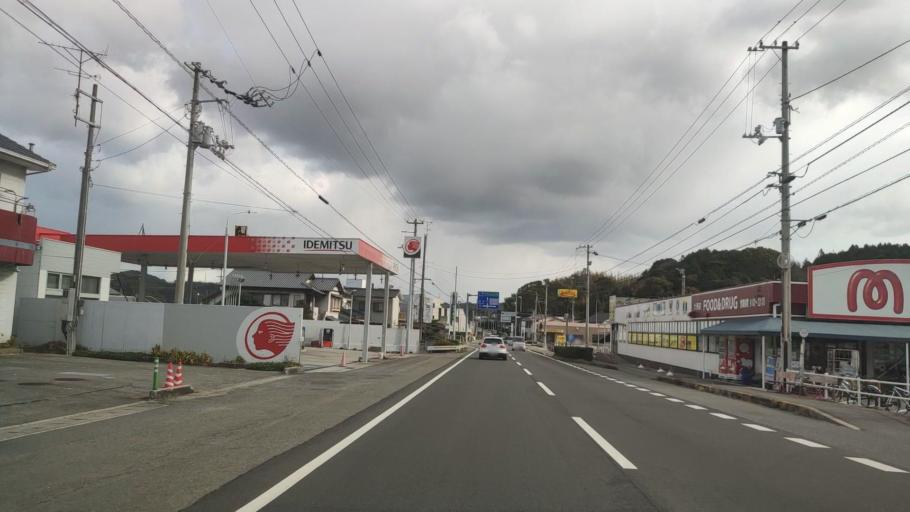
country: JP
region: Ehime
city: Hojo
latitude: 34.0622
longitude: 132.9256
